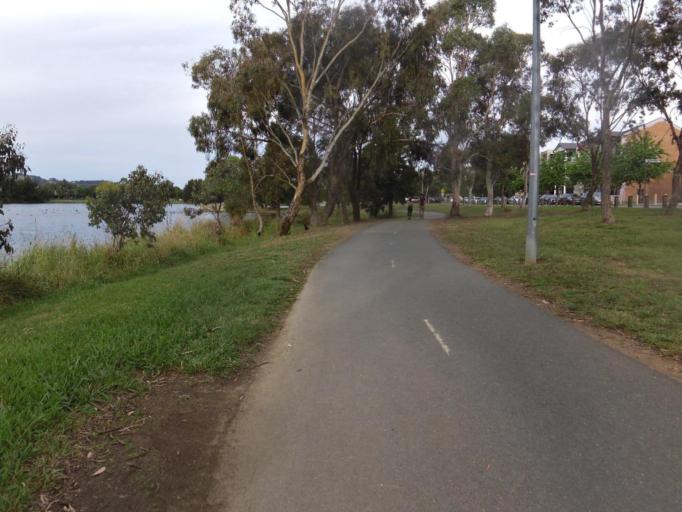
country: AU
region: Australian Capital Territory
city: Kaleen
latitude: -35.1767
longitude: 149.1327
